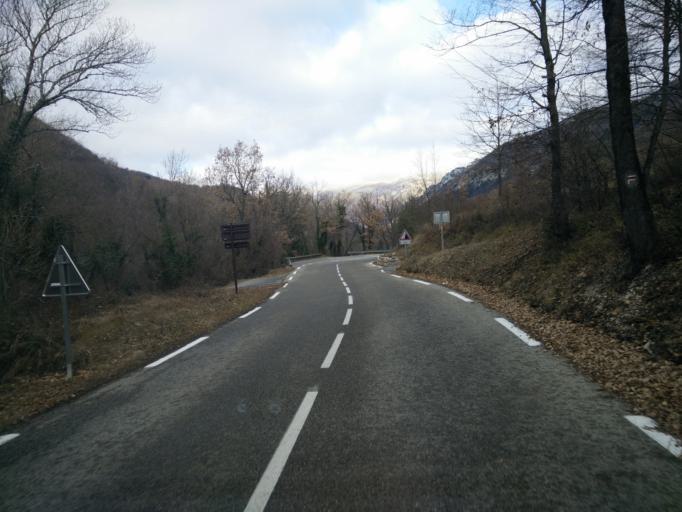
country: FR
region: Provence-Alpes-Cote d'Azur
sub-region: Departement des Alpes-Maritimes
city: Tourrettes-sur-Loup
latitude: 43.7623
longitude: 6.9879
